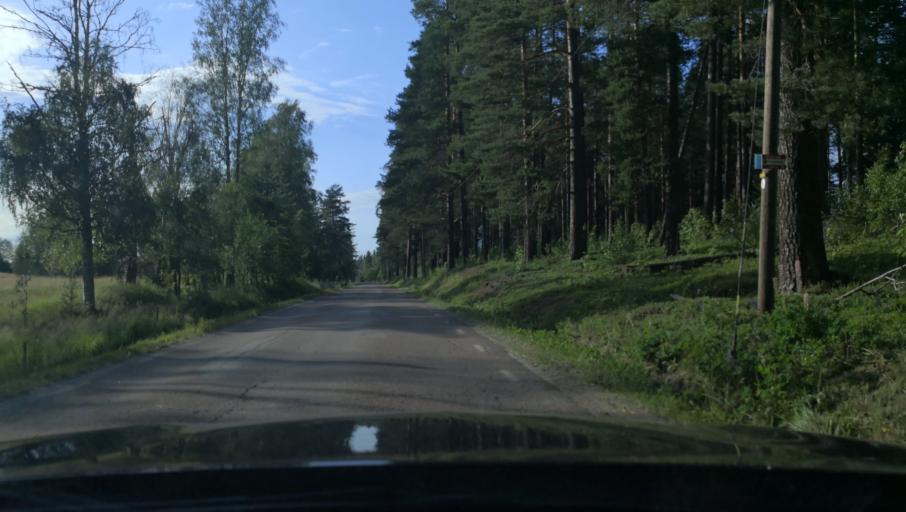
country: SE
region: Dalarna
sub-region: Smedjebackens Kommun
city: Smedjebacken
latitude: 60.0350
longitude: 15.3266
